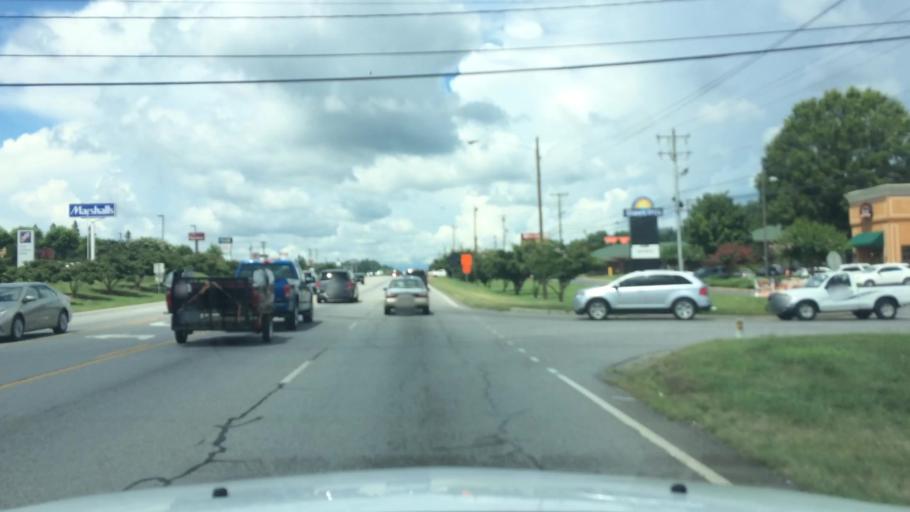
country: US
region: North Carolina
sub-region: Wilkes County
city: Cricket
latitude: 36.1503
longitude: -81.1963
